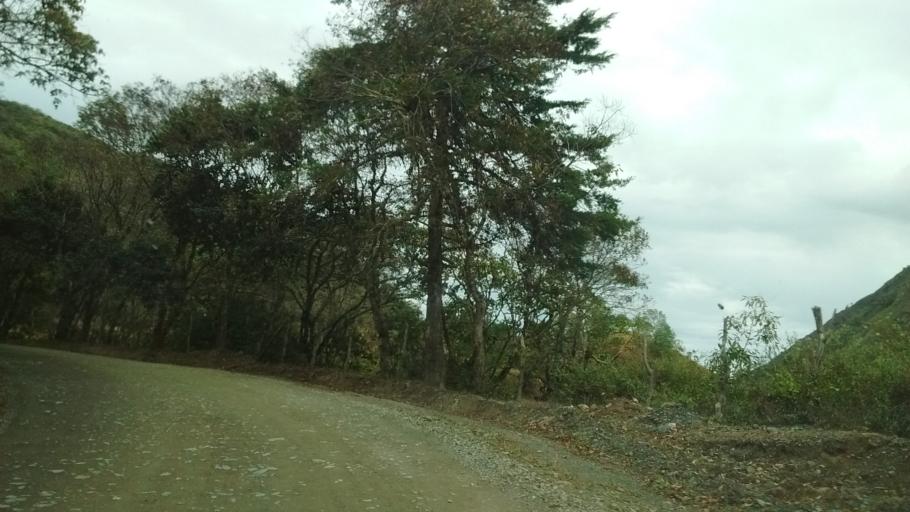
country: CO
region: Cauca
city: Almaguer
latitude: 1.8535
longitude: -76.9494
